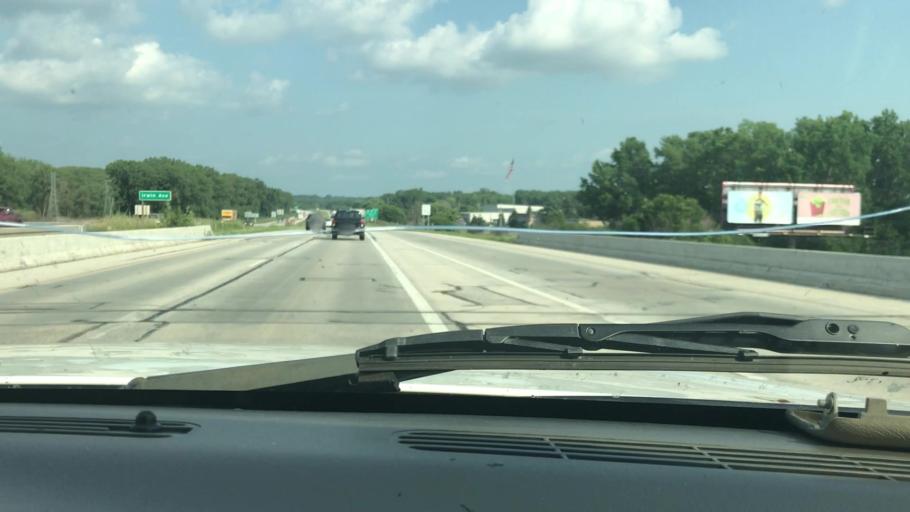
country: US
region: Wisconsin
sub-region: Brown County
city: Green Bay
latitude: 44.5259
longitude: -87.9857
